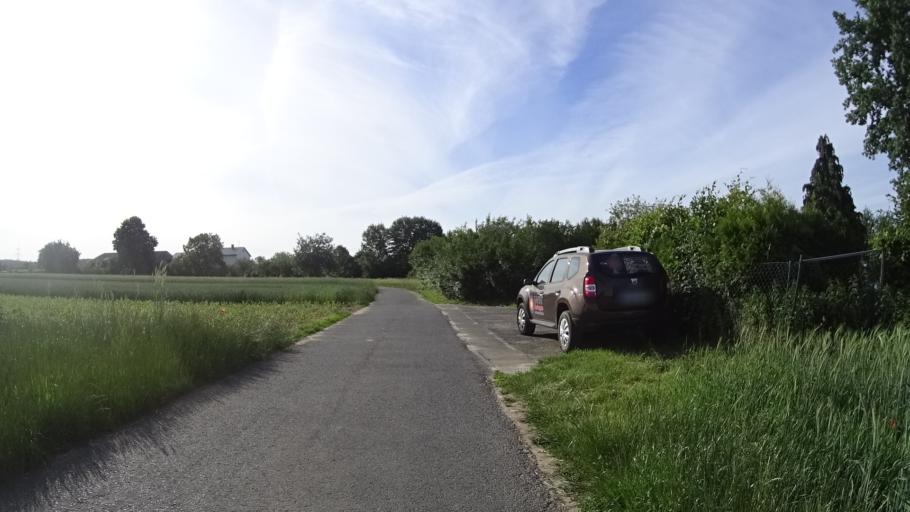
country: DE
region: Bavaria
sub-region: Regierungsbezirk Unterfranken
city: Kleinostheim
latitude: 50.0096
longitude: 9.0445
